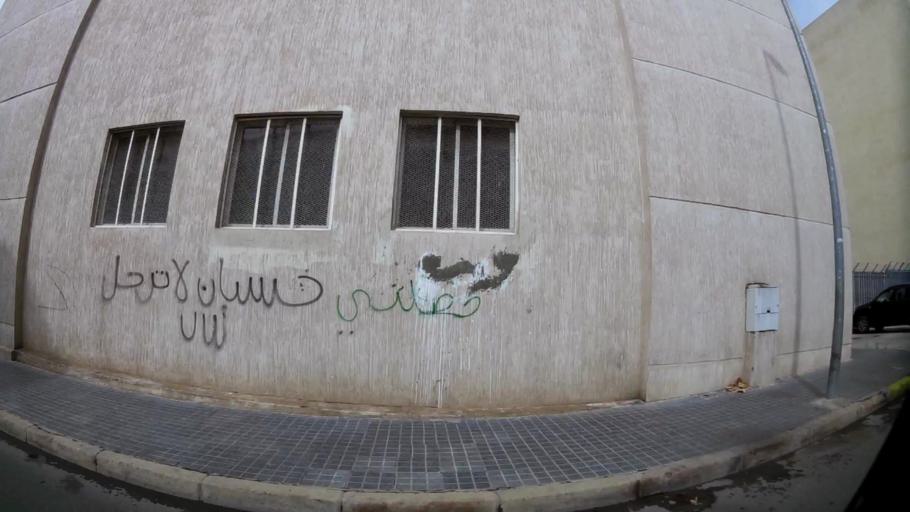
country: MA
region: Grand Casablanca
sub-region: Mohammedia
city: Mohammedia
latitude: 33.6862
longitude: -7.3761
